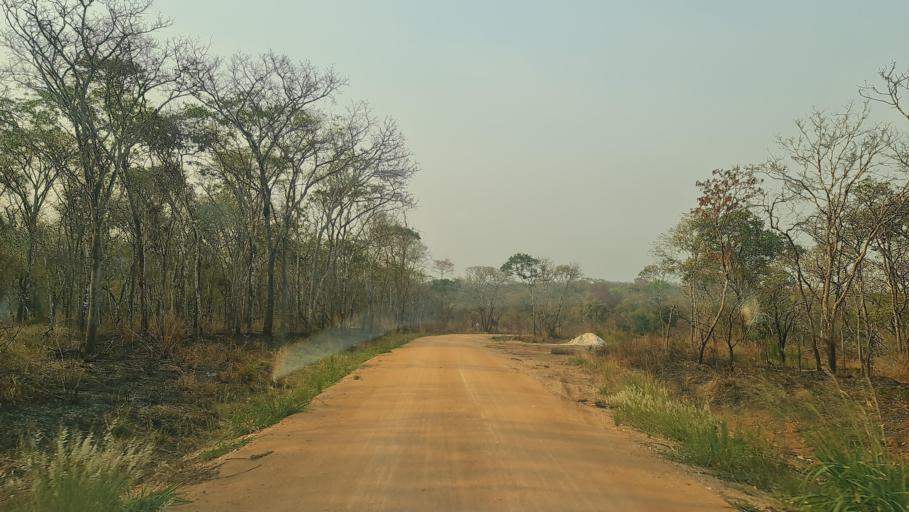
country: MZ
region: Zambezia
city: Quelimane
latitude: -17.1425
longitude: 37.1356
